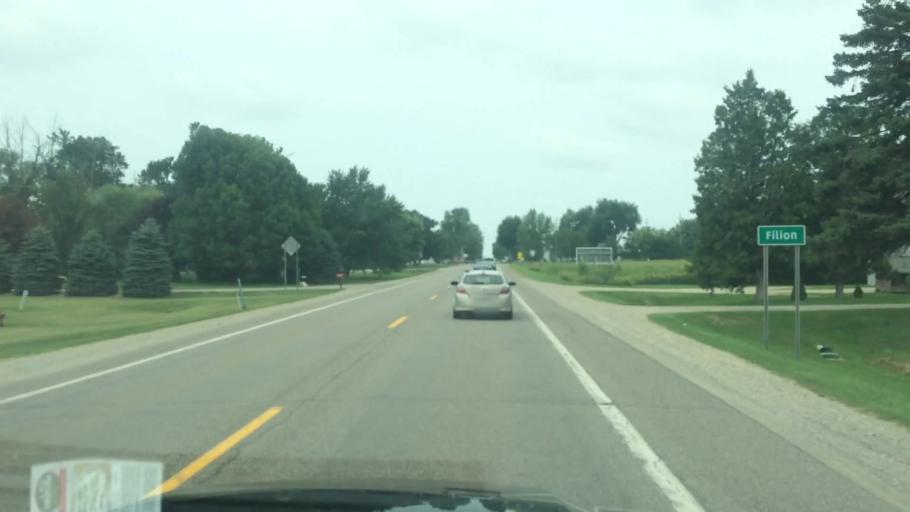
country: US
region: Michigan
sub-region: Huron County
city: Bad Axe
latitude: 43.8921
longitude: -83.0032
